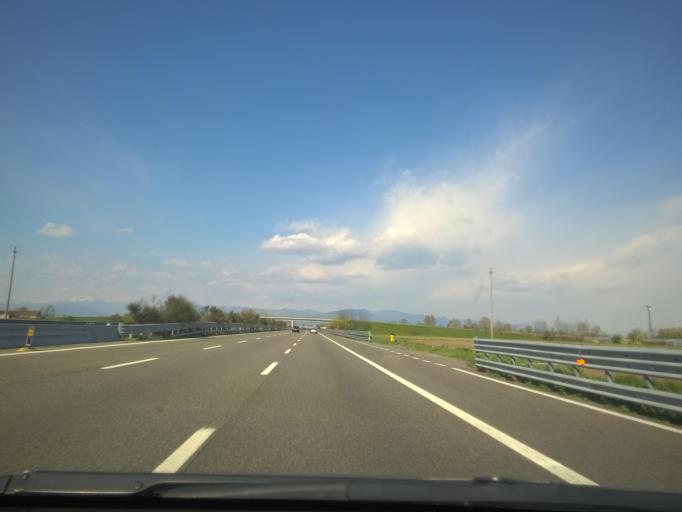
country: IT
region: Lombardy
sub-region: Provincia di Brescia
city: Bagnolo Mella
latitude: 45.4044
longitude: 10.1897
